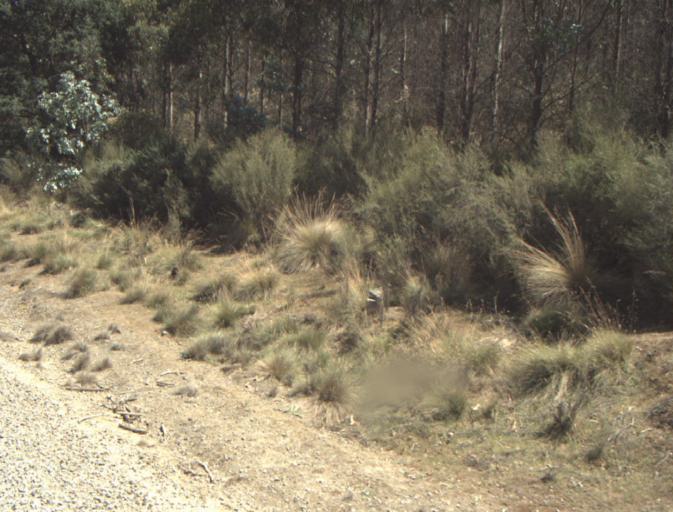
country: AU
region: Tasmania
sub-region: Dorset
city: Scottsdale
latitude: -41.3081
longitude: 147.4658
